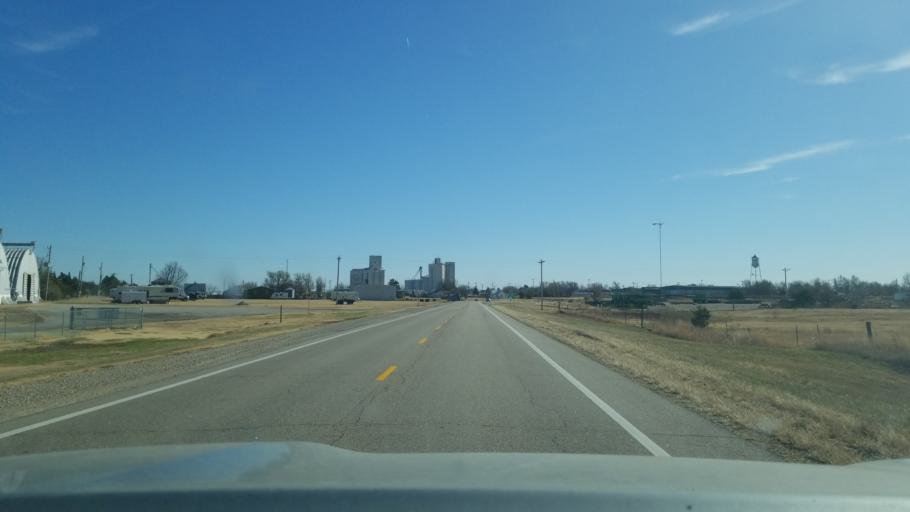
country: US
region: Kansas
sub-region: Kiowa County
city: Greensburg
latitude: 37.5546
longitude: -99.6409
